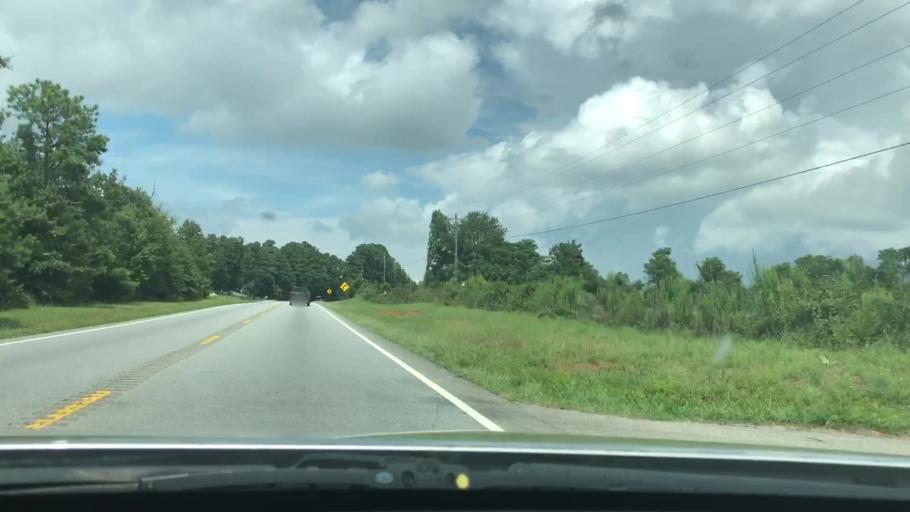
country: US
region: Georgia
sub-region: Lamar County
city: Barnesville
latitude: 33.1326
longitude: -84.1539
